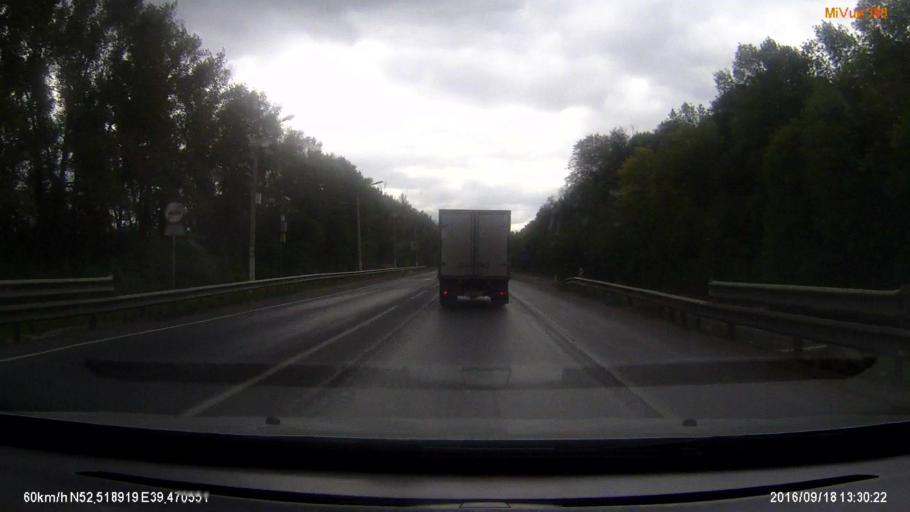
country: RU
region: Lipetsk
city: Borinskoye
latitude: 52.4699
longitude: 39.4194
